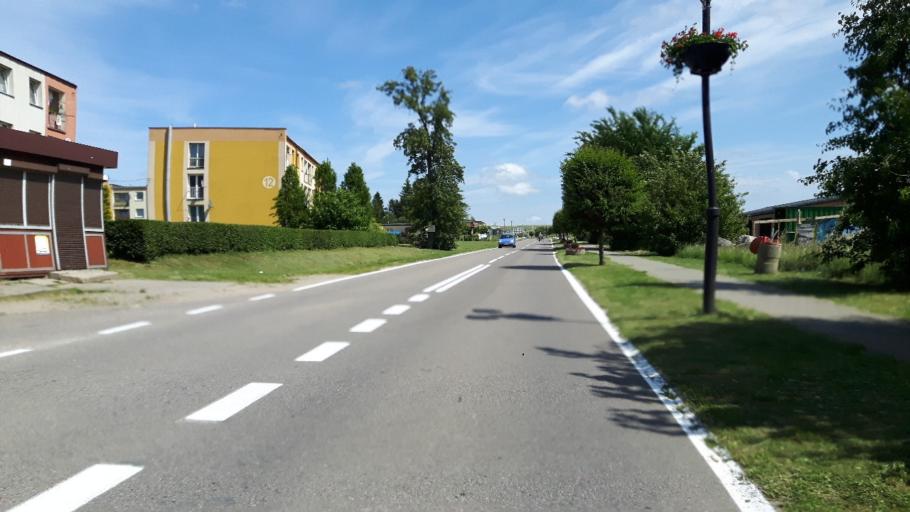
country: PL
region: Pomeranian Voivodeship
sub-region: Powiat wejherowski
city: Gniewino
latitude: 54.7162
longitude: 18.0275
